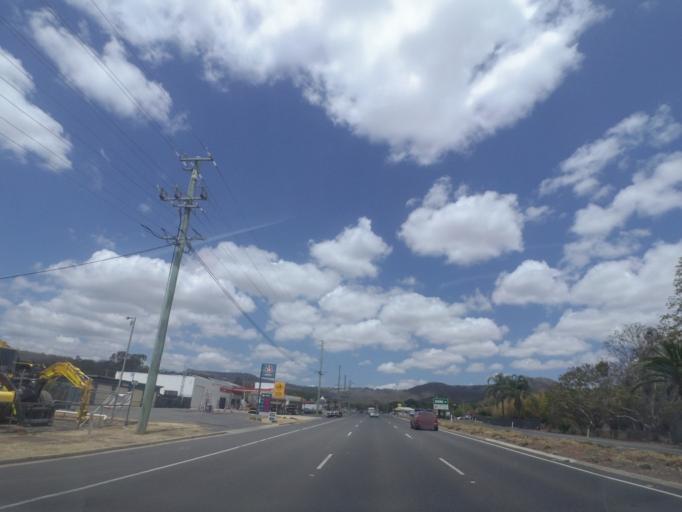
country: AU
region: Queensland
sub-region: Toowoomba
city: East Toowoomba
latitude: -27.5533
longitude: 152.0260
